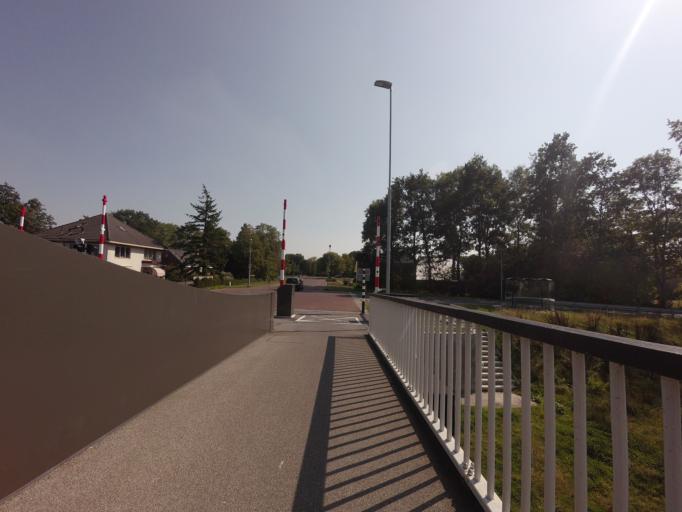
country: NL
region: Groningen
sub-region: Gemeente Zuidhorn
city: Noordhorn
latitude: 53.2550
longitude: 6.3998
